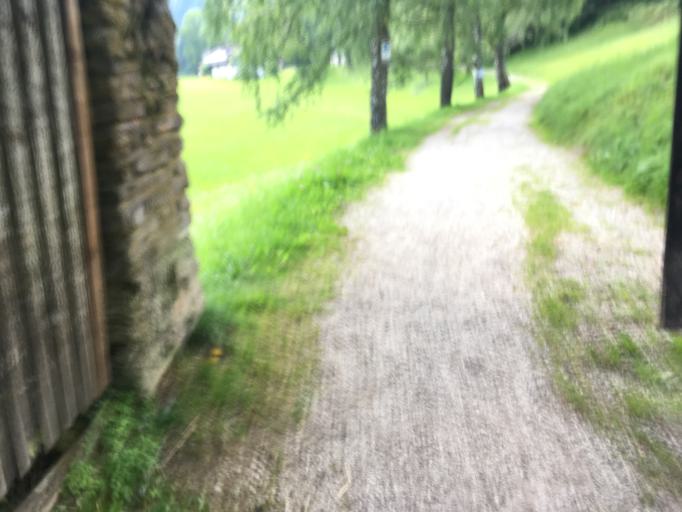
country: AT
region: Lower Austria
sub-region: Politischer Bezirk Lilienfeld
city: Mitterbach am Erlaufsee
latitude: 47.7954
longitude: 15.2618
